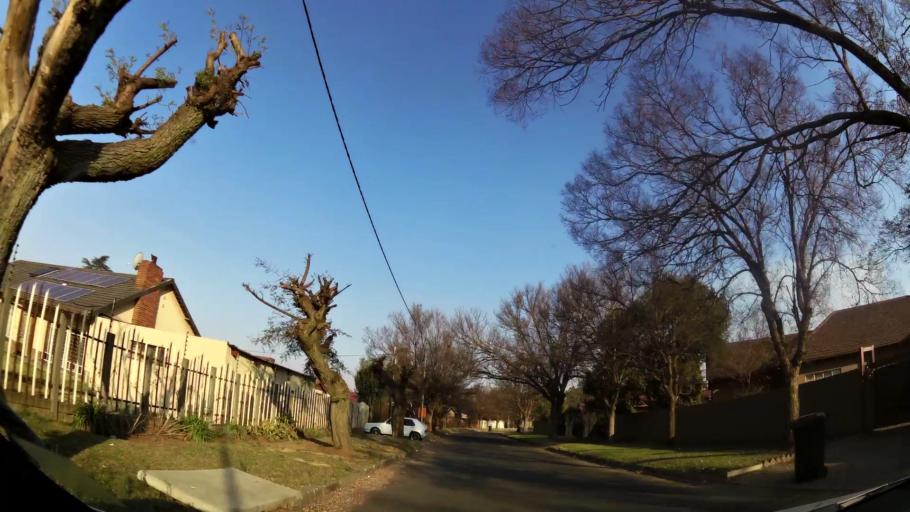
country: ZA
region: Gauteng
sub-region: Ekurhuleni Metropolitan Municipality
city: Springs
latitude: -26.2568
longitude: 28.3934
